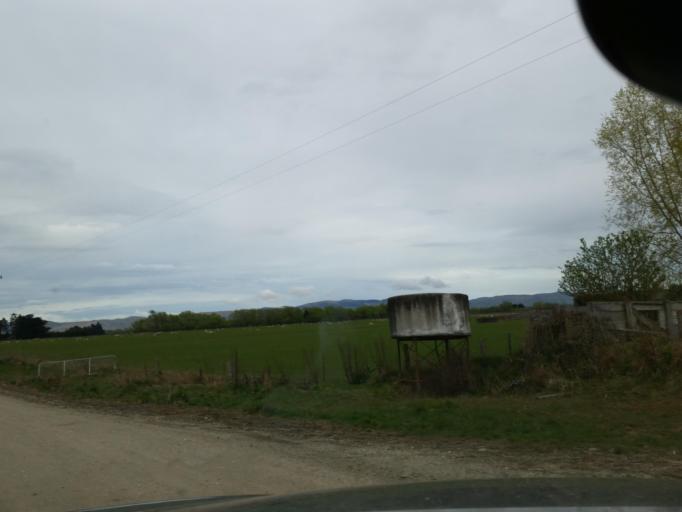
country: NZ
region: Southland
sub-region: Gore District
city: Gore
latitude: -45.8438
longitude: 168.7390
